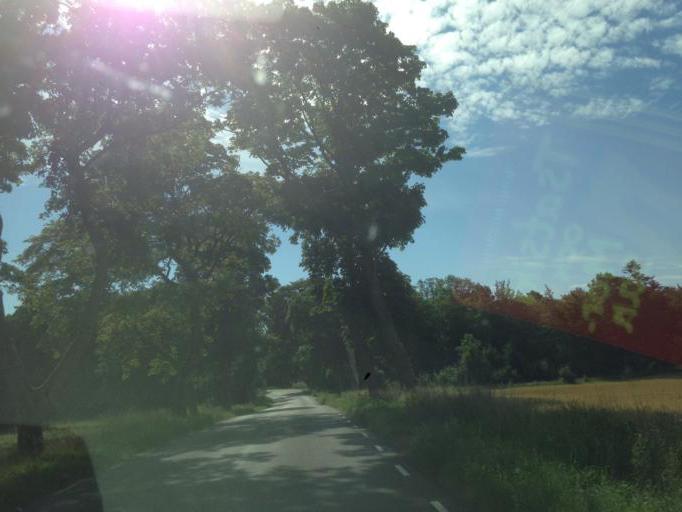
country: SE
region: Skane
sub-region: Tomelilla Kommun
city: Tomelilla
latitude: 55.6452
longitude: 14.0419
